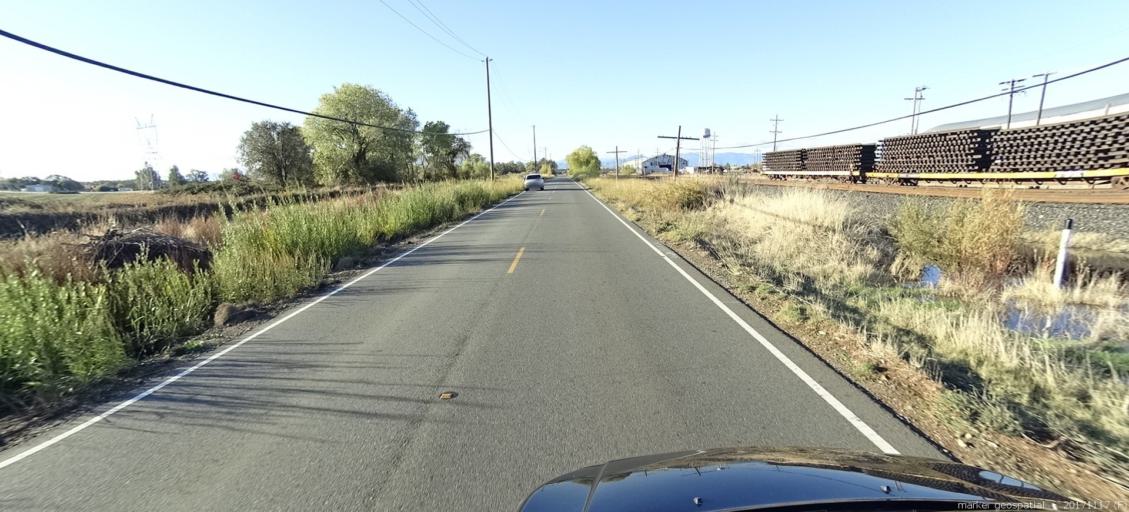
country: US
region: California
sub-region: Shasta County
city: Anderson
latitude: 40.4331
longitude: -122.2758
